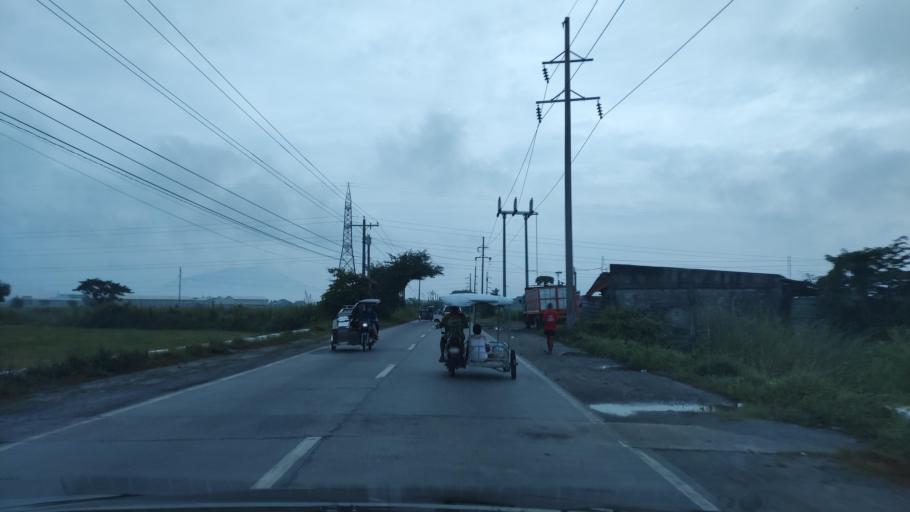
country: PH
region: Central Luzon
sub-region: Province of Pampanga
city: Laug
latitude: 15.0514
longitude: 120.7523
